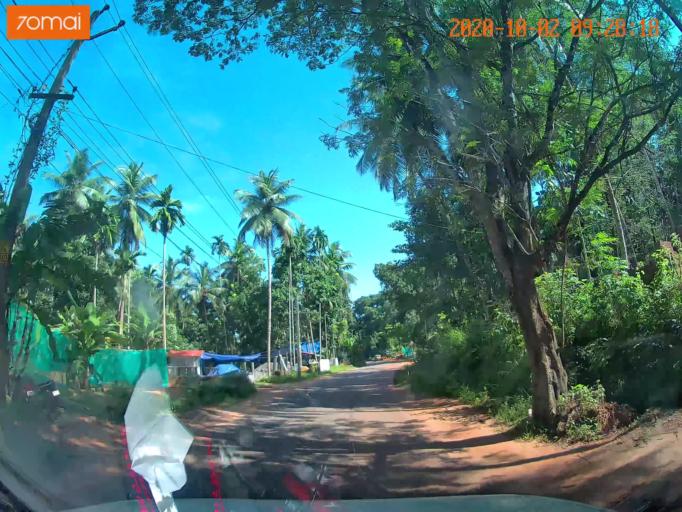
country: IN
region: Kerala
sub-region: Kozhikode
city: Naduvannur
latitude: 11.6056
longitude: 75.7635
